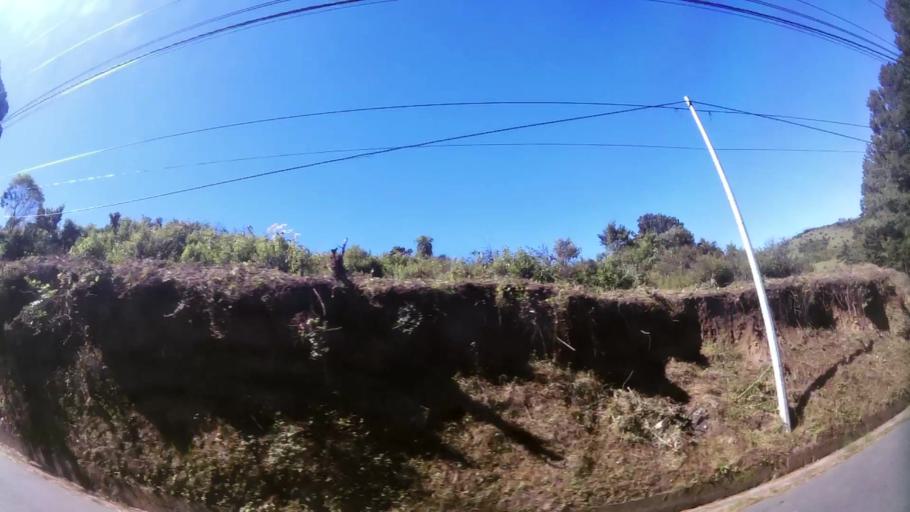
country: GT
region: Guatemala
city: San Jose Pinula
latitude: 14.5151
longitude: -90.4241
